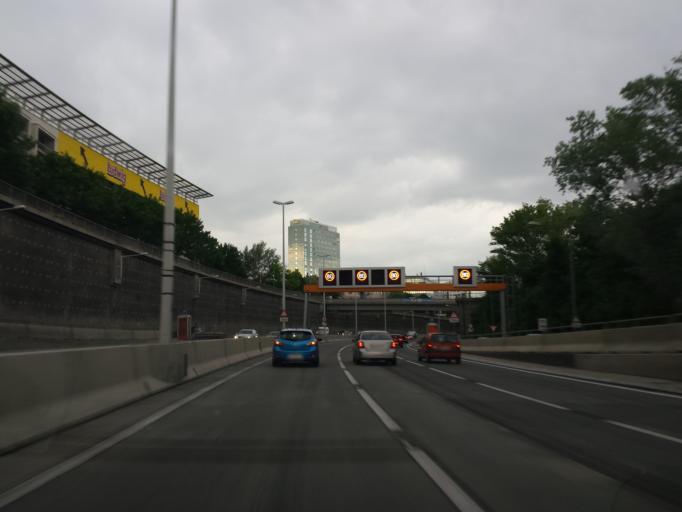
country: AT
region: Vienna
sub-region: Wien Stadt
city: Vienna
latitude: 48.1639
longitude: 16.3860
